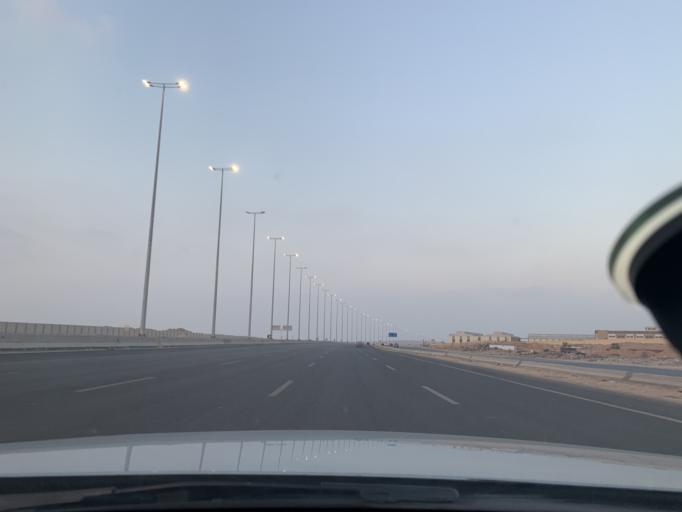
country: EG
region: Muhafazat al Qalyubiyah
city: Al Khankah
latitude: 30.0877
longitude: 31.4600
